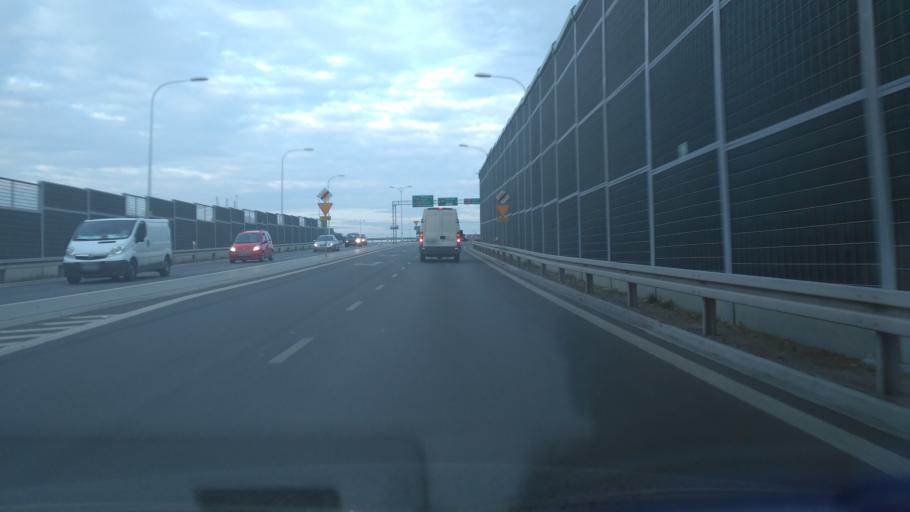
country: PL
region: Lublin Voivodeship
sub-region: Powiat lubelski
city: Jakubowice Murowane
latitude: 51.2748
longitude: 22.6495
